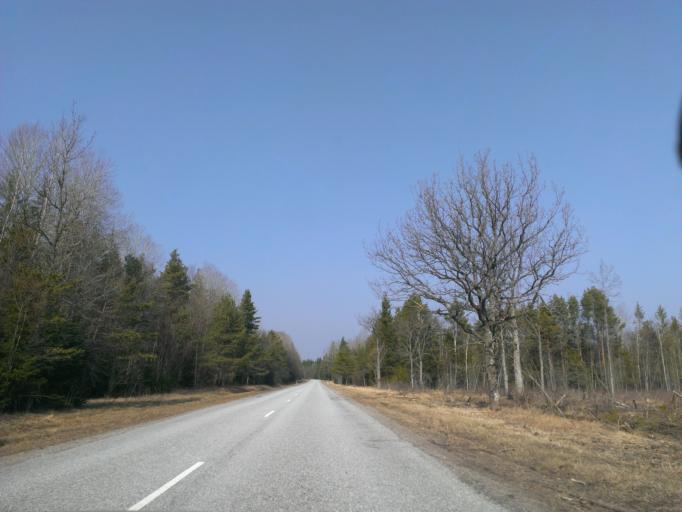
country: EE
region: Saare
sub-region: Kuressaare linn
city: Kuressaare
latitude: 58.3548
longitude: 22.6747
